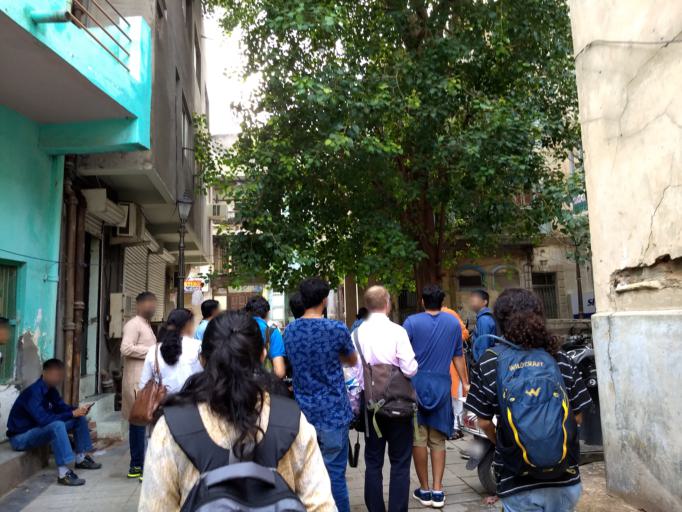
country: IN
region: Gujarat
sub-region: Ahmadabad
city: Ahmedabad
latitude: 23.0282
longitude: 72.5919
